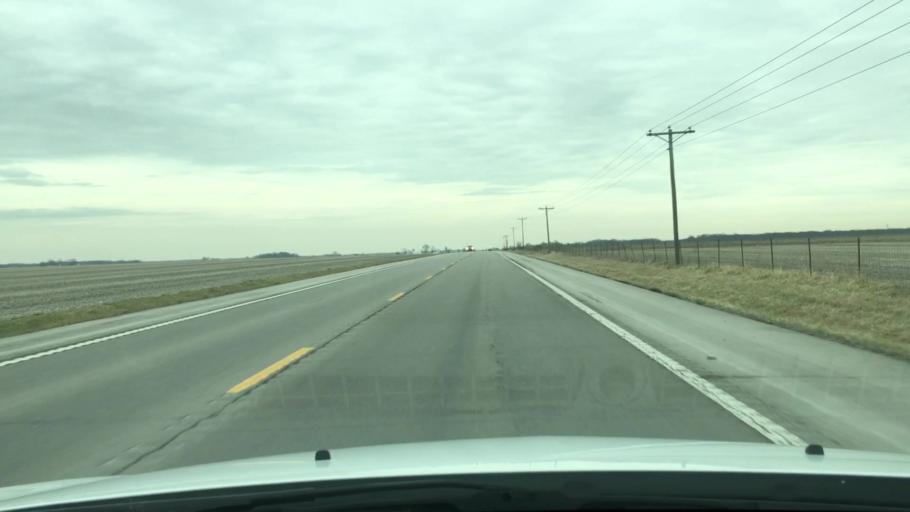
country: US
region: Missouri
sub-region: Audrain County
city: Mexico
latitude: 39.1640
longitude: -91.7348
